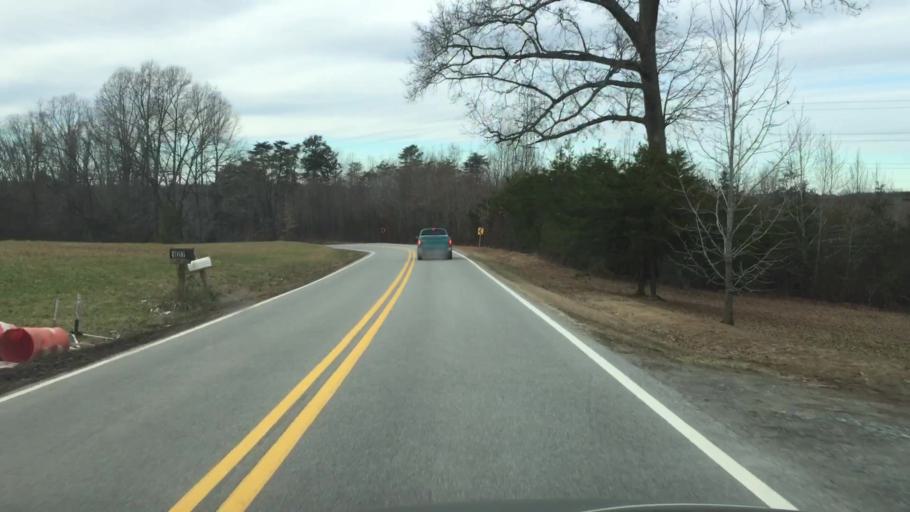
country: US
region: North Carolina
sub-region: Rockingham County
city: Reidsville
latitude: 36.3933
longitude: -79.6570
